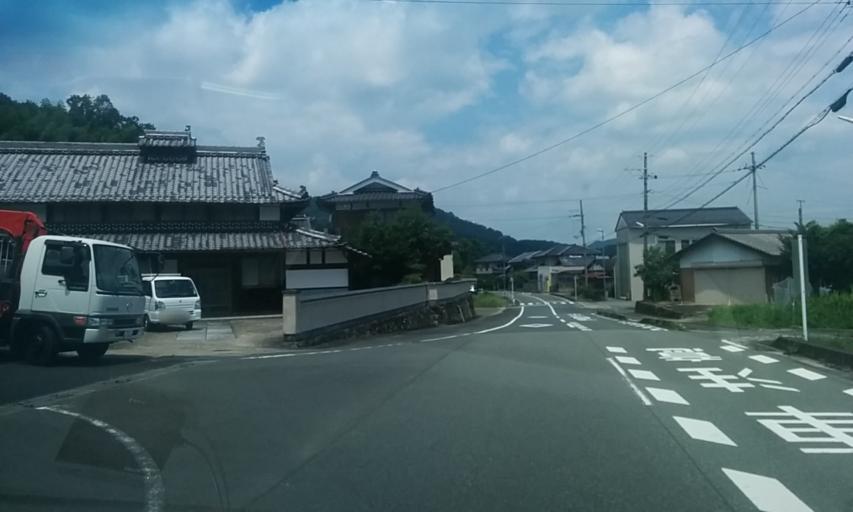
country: JP
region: Kyoto
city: Ayabe
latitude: 35.1955
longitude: 135.2473
